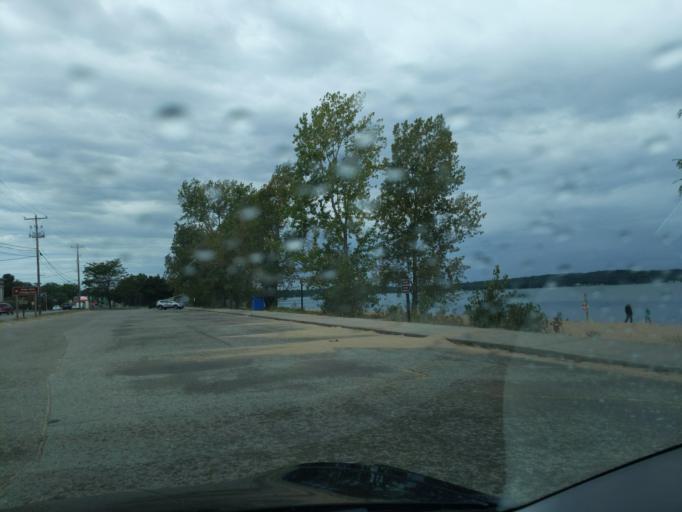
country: US
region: Michigan
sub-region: Grand Traverse County
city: Traverse City
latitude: 44.7481
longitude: -85.5529
